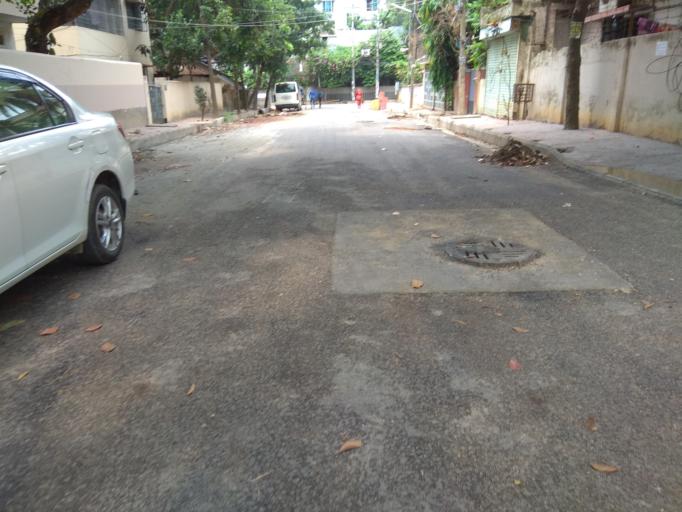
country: BD
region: Dhaka
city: Azimpur
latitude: 23.8033
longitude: 90.3576
